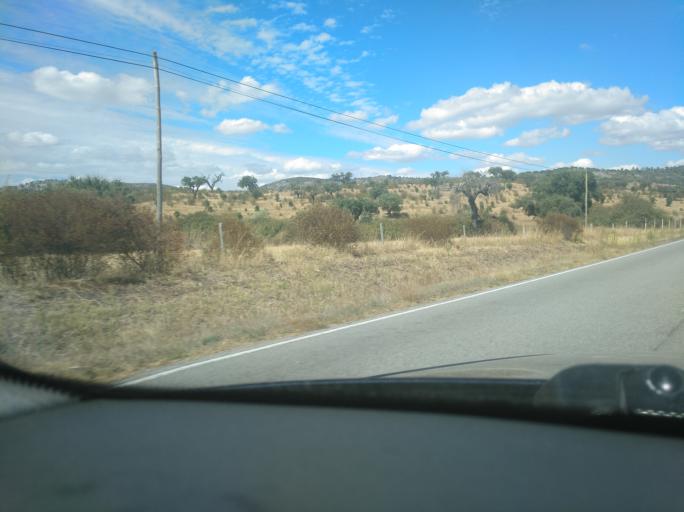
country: PT
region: Portalegre
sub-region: Arronches
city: Arronches
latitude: 39.1476
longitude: -7.2174
